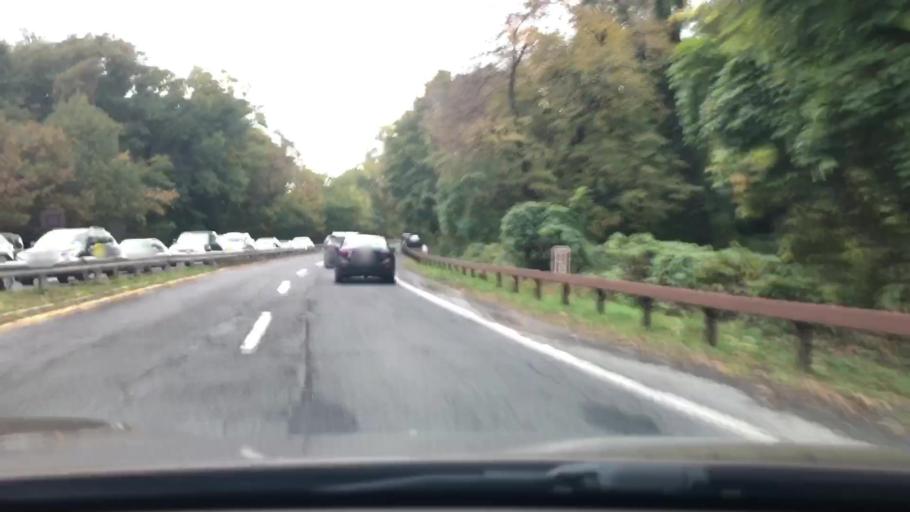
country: US
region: New York
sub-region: Westchester County
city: Tuckahoe
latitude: 40.9689
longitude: -73.8172
